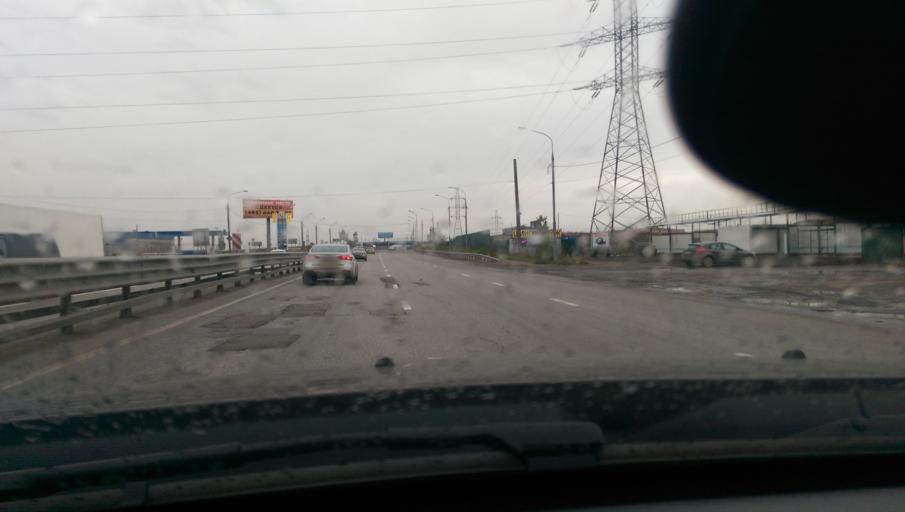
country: RU
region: Moscow
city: Vatutino
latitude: 55.9170
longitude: 37.6671
